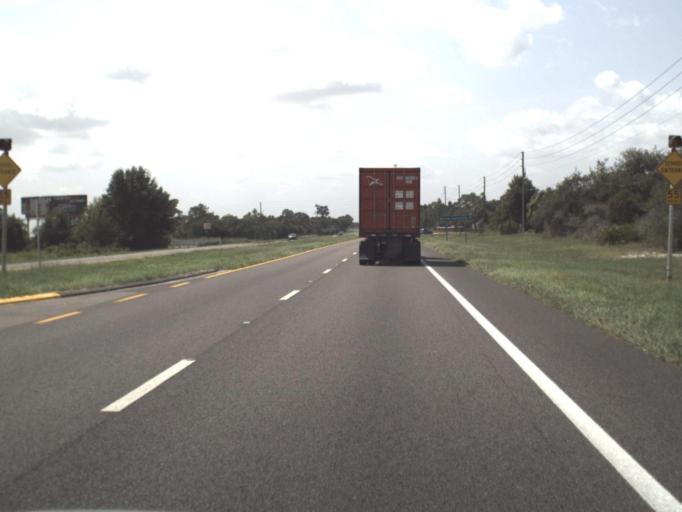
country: US
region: Florida
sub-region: Polk County
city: Crooked Lake Park
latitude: 27.8285
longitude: -81.5921
